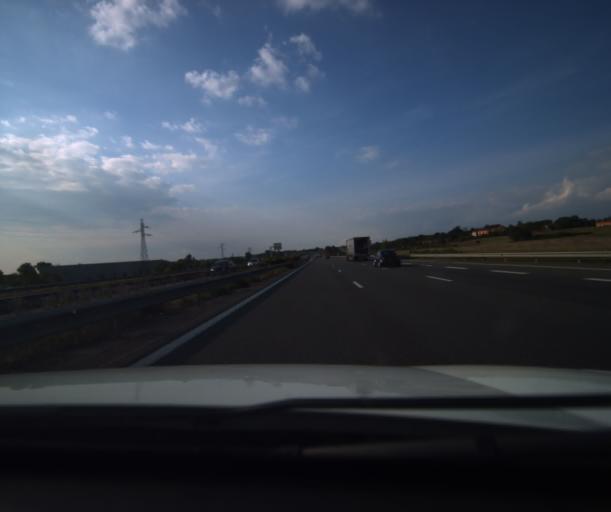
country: FR
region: Midi-Pyrenees
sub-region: Departement de la Haute-Garonne
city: Bouloc
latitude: 43.7679
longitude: 1.3852
